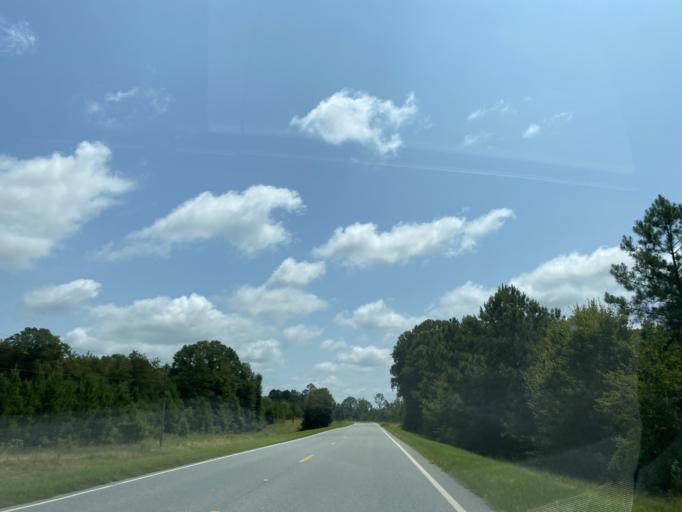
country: US
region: Georgia
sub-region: Telfair County
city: Helena
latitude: 32.0296
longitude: -83.0137
